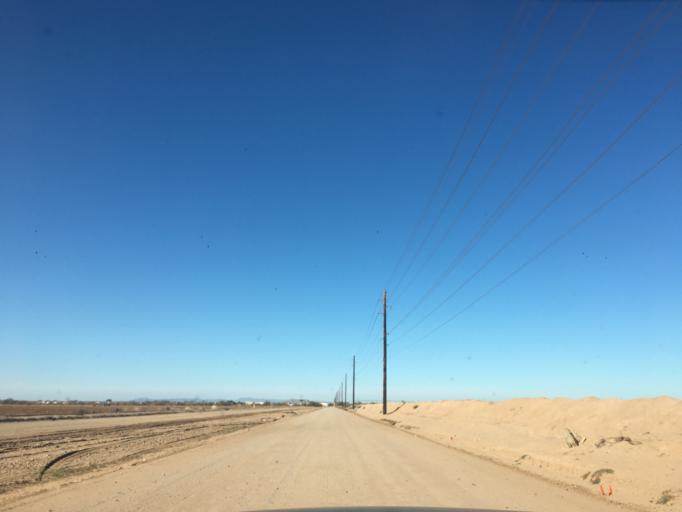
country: US
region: Arizona
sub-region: Pinal County
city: Maricopa
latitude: 33.0205
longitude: -112.0138
